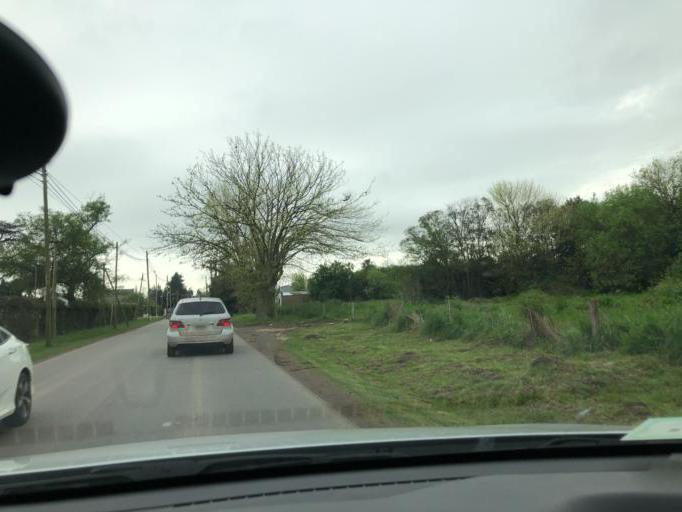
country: AR
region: Buenos Aires
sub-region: Partido de La Plata
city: La Plata
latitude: -34.8973
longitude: -58.0672
